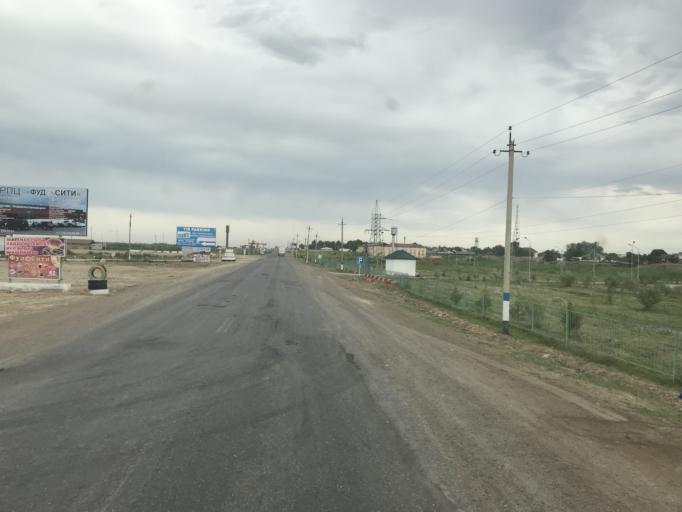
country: KZ
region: Ongtustik Qazaqstan
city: Asykata
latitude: 40.9627
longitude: 68.4599
